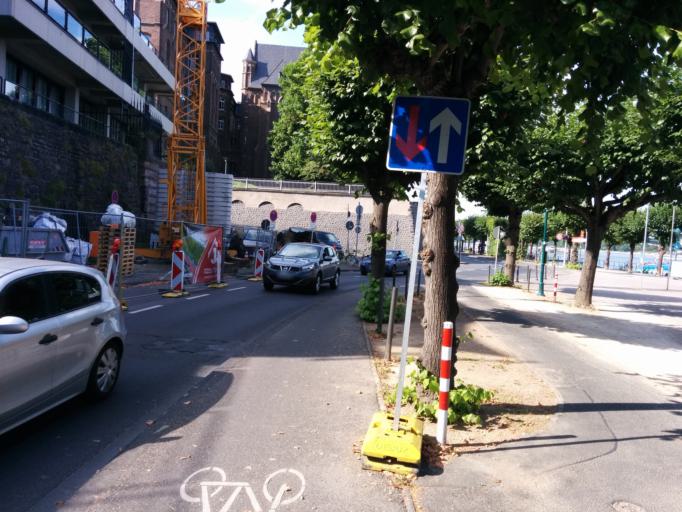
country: DE
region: North Rhine-Westphalia
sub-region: Regierungsbezirk Koln
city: Bonn
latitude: 50.7317
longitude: 7.1094
